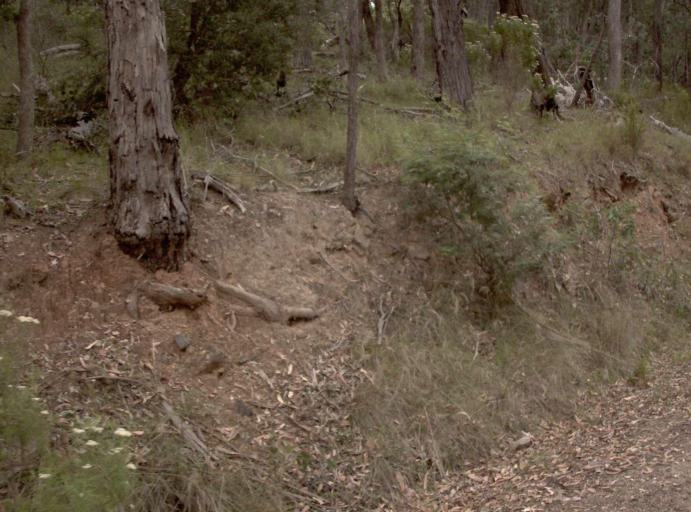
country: AU
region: Victoria
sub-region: East Gippsland
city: Bairnsdale
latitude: -37.6924
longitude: 147.2932
